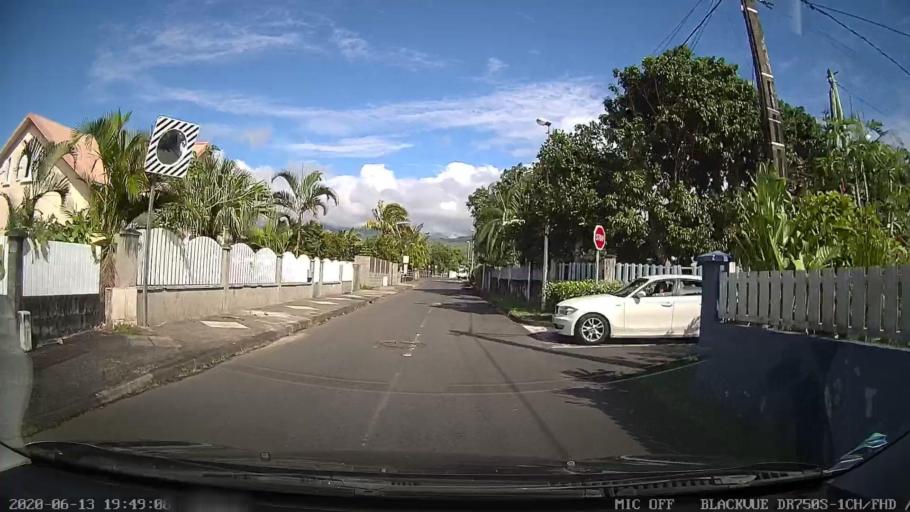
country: RE
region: Reunion
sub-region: Reunion
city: Bras-Panon
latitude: -21.0039
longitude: 55.6897
